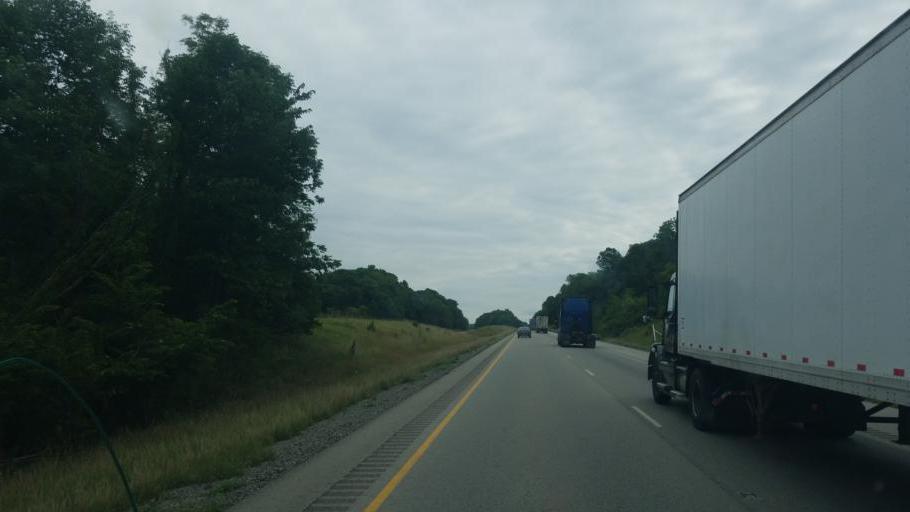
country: US
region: Indiana
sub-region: Putnam County
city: Cloverdale
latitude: 39.5144
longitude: -86.9191
